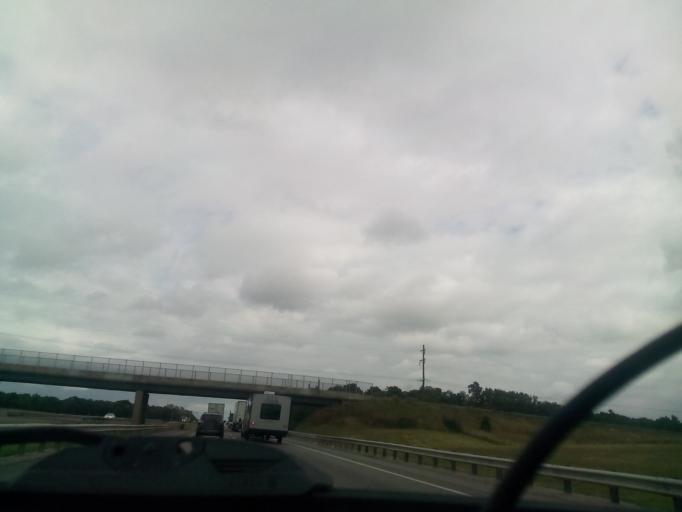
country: US
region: Ohio
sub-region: Williams County
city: Montpelier
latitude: 41.6288
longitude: -84.7482
